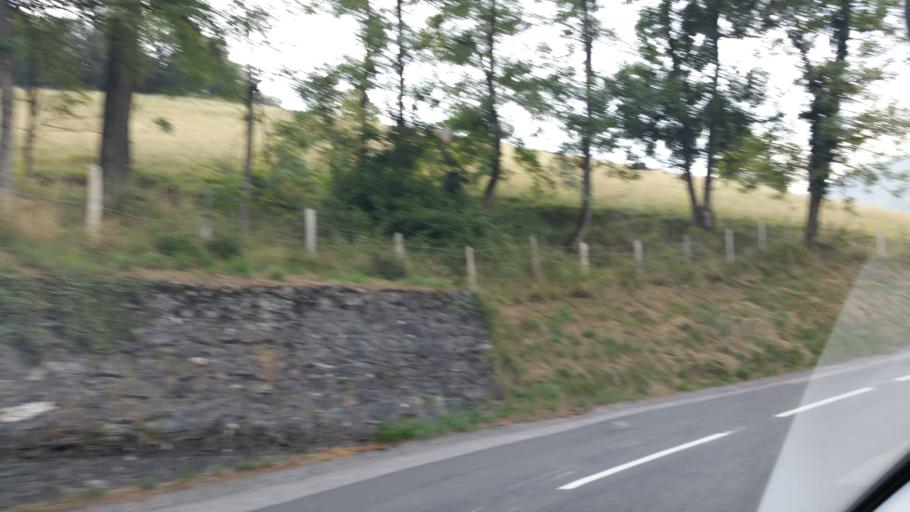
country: FR
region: Rhone-Alpes
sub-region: Departement de la Savoie
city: Aiton
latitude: 45.5627
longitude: 6.2543
